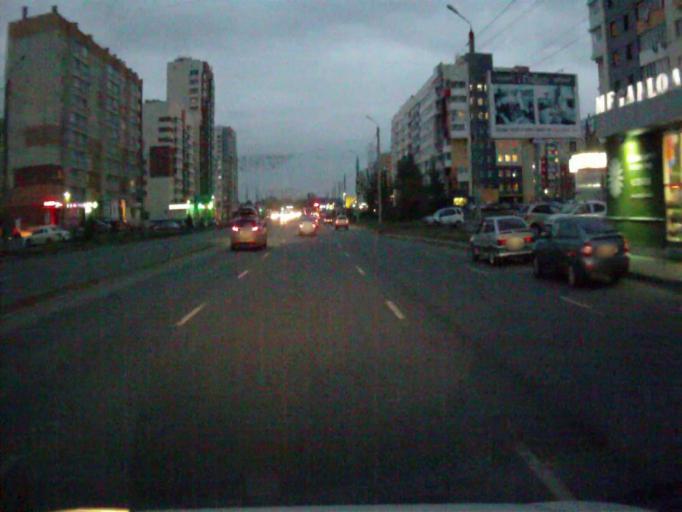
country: RU
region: Chelyabinsk
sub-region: Gorod Chelyabinsk
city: Chelyabinsk
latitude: 55.1664
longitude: 61.2948
